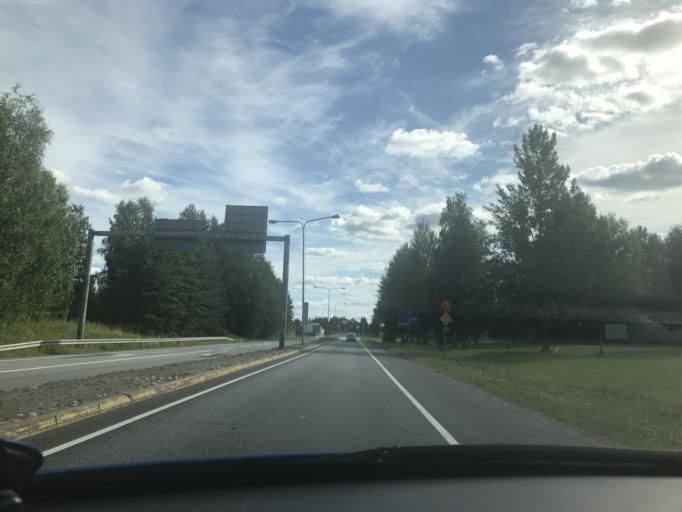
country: FI
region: Southern Ostrobothnia
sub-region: Kuusiokunnat
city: Alavus
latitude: 62.5915
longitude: 23.6130
